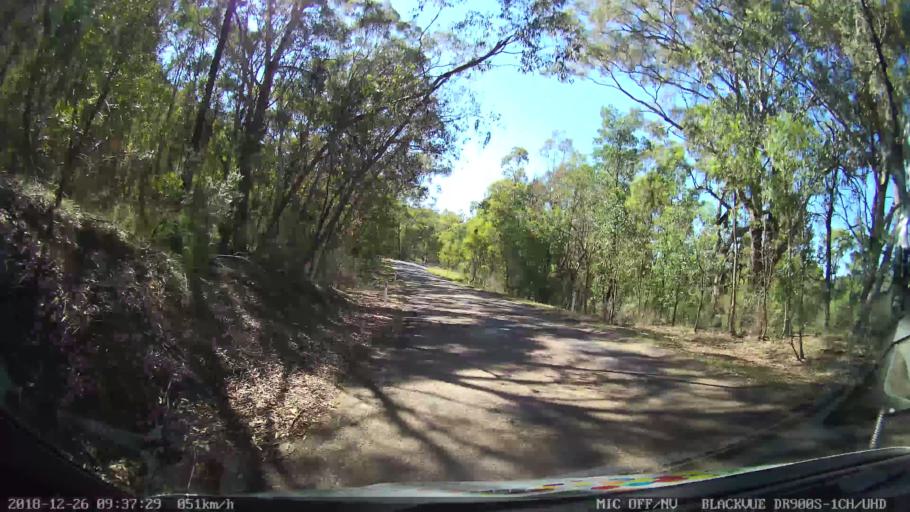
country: AU
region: New South Wales
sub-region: Mid-Western Regional
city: Kandos
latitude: -32.9327
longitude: 150.0404
